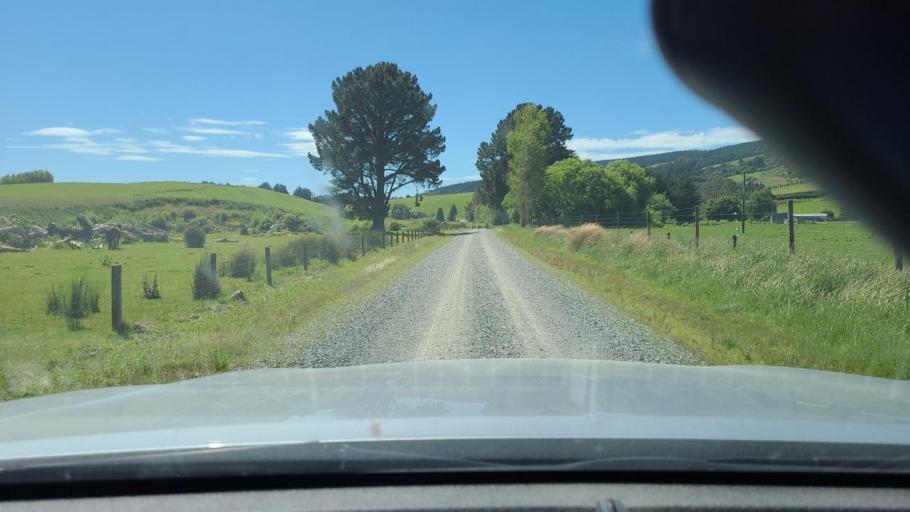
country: NZ
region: Southland
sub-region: Southland District
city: Riverton
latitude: -46.0580
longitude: 167.8545
